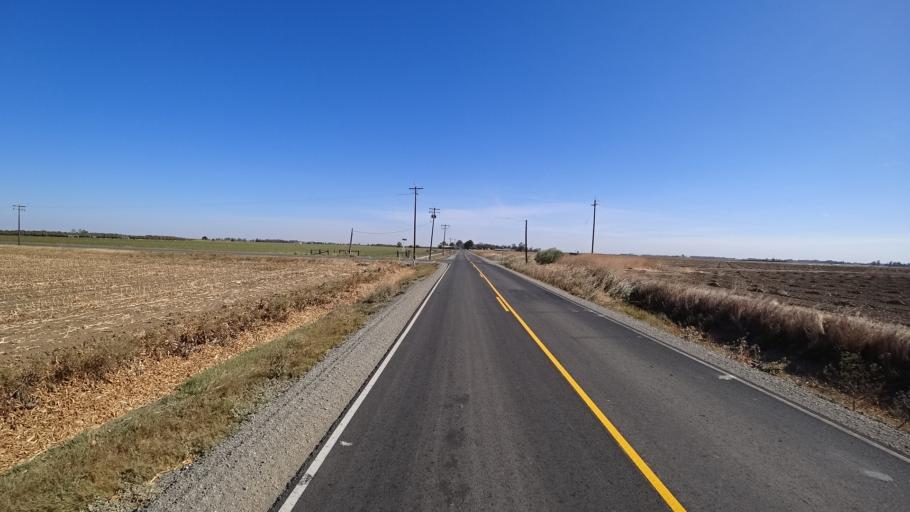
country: US
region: California
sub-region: Yolo County
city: Cottonwood
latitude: 38.6199
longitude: -121.8961
